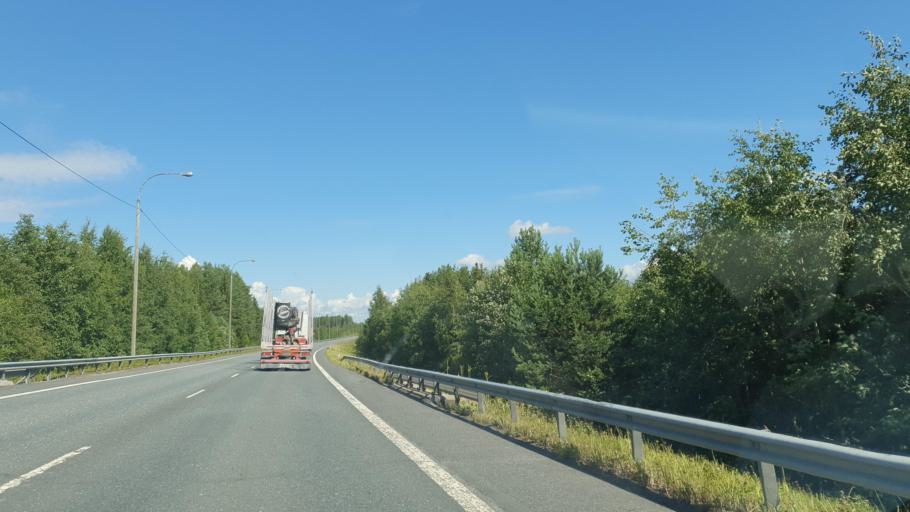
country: FI
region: Northern Savo
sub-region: Ylae-Savo
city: Iisalmi
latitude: 63.6055
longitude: 27.2156
